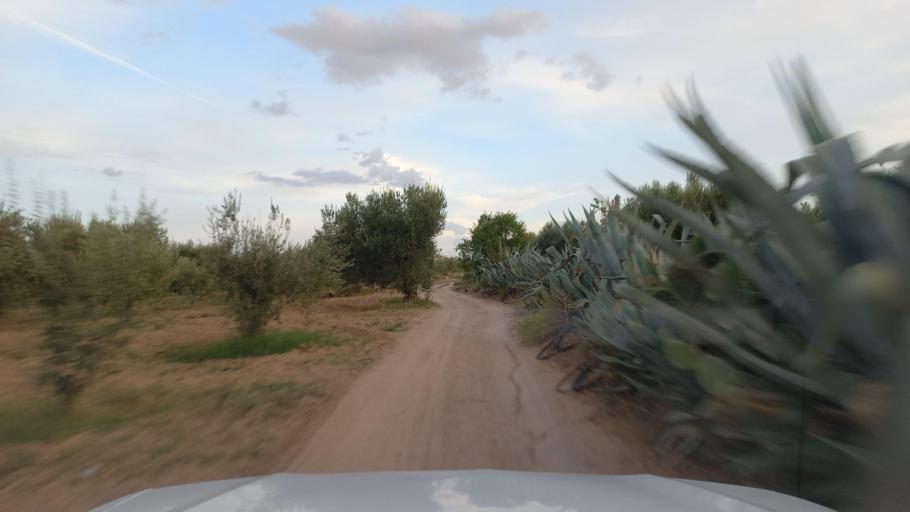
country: TN
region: Al Qasrayn
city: Sbiba
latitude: 35.4111
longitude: 9.1036
